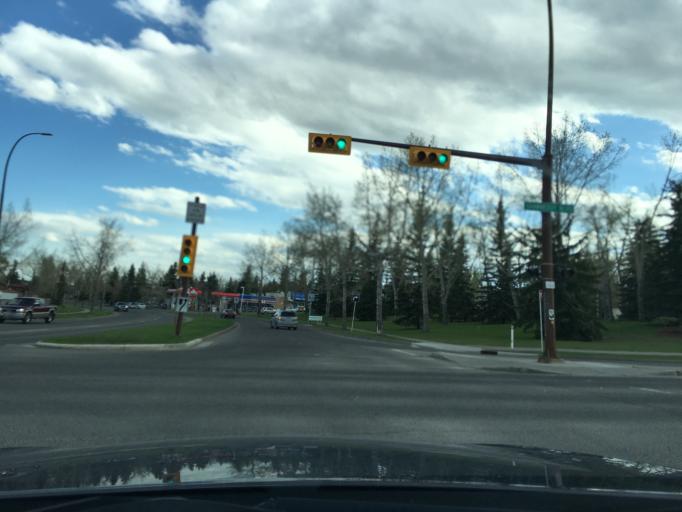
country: CA
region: Alberta
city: Calgary
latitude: 50.9130
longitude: -114.0740
